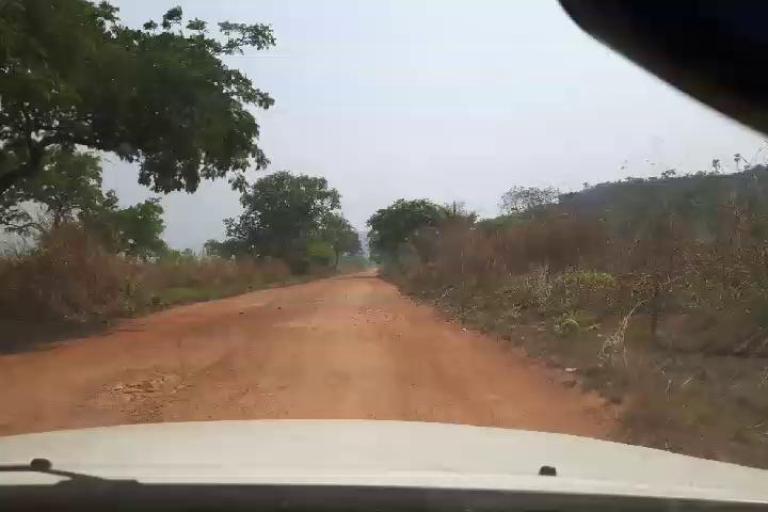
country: SL
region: Northern Province
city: Bumbuna
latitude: 8.9316
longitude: -11.8187
